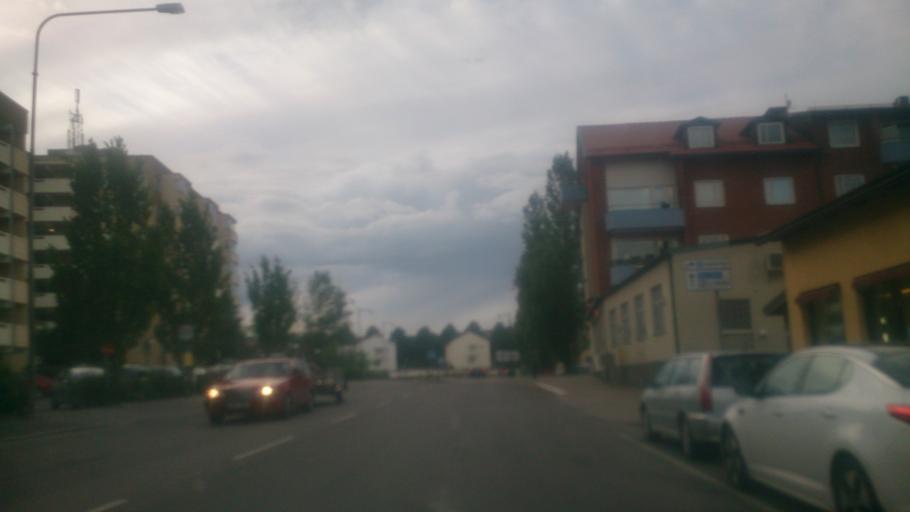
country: SE
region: OEstergoetland
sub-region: Motala Kommun
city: Motala
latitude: 58.5366
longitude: 15.0328
